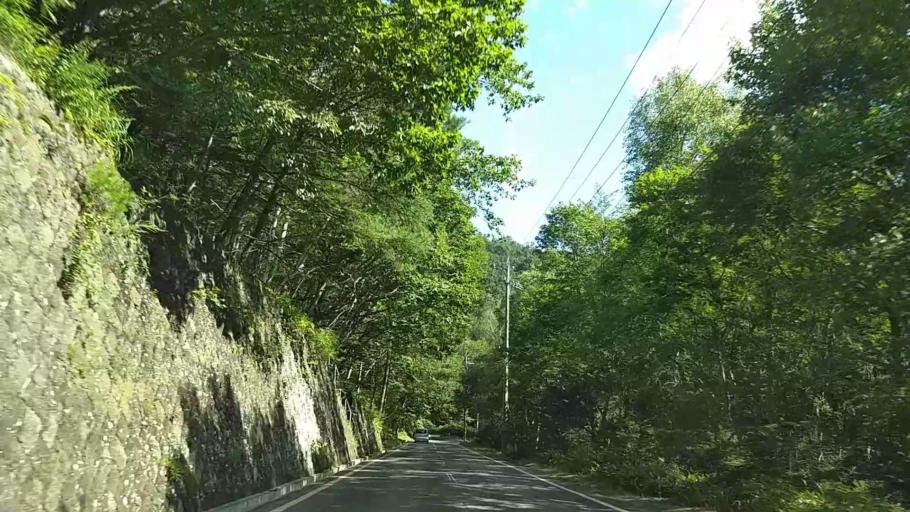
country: JP
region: Nagano
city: Chino
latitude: 36.1227
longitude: 138.2709
